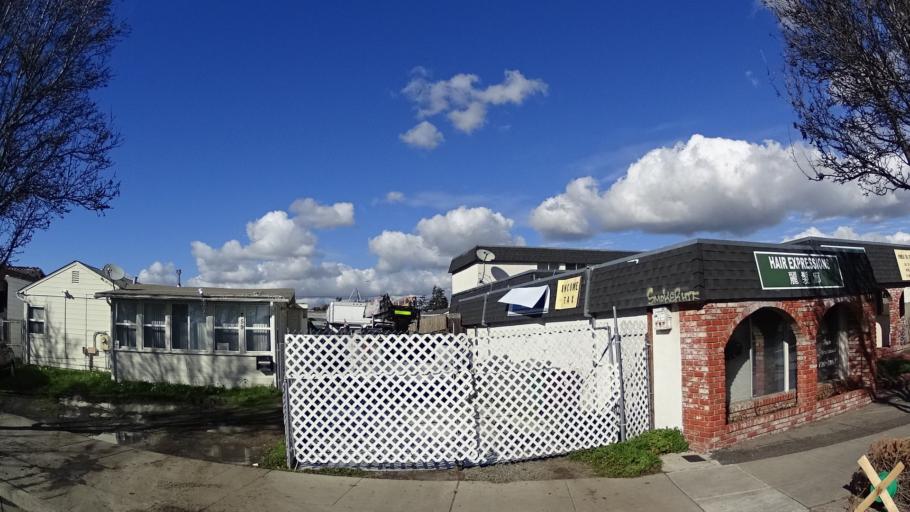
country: US
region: California
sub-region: Alameda County
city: Cherryland
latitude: 37.6660
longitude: -122.1142
